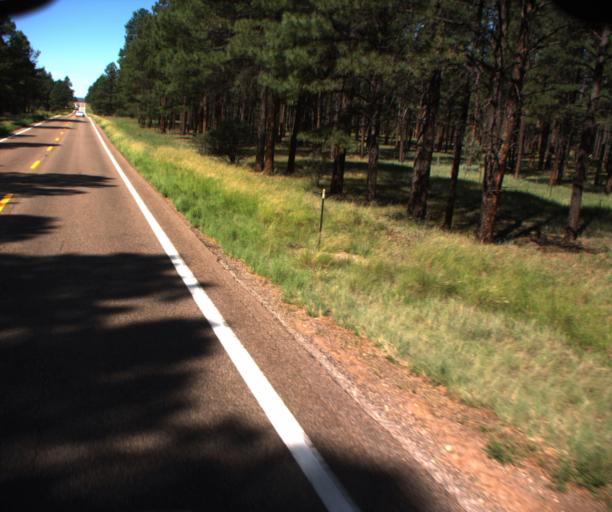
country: US
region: Arizona
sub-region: Navajo County
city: Lake of the Woods
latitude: 34.1228
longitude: -110.1229
